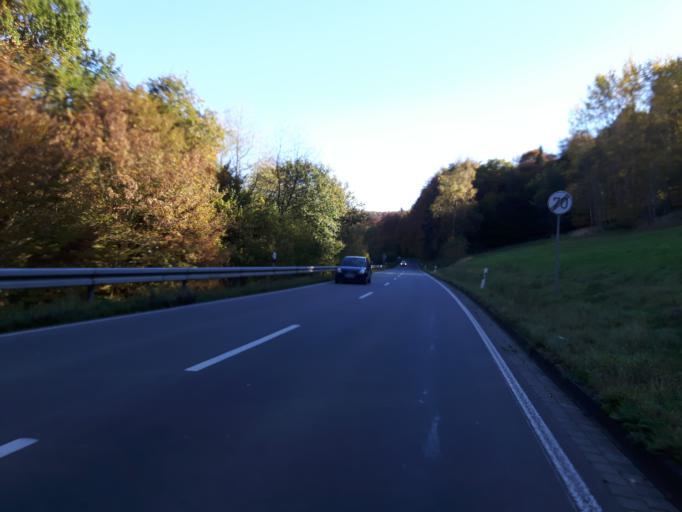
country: DE
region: Bavaria
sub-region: Regierungsbezirk Unterfranken
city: Leidersbach
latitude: 49.8960
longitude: 9.2507
